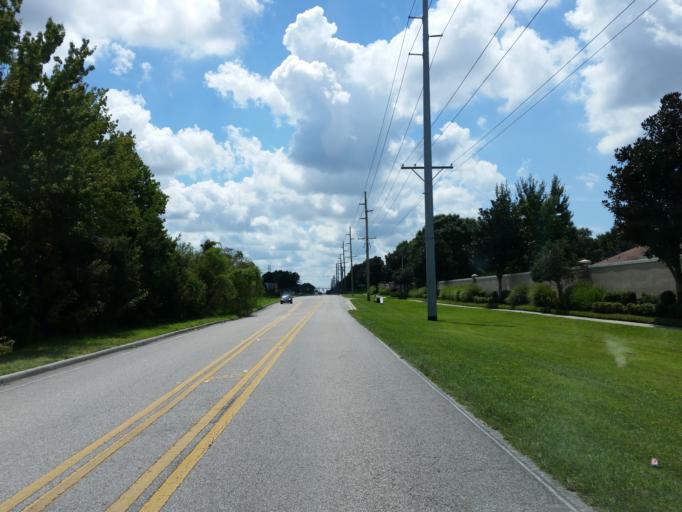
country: US
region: Florida
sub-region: Hillsborough County
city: Riverview
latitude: 27.8602
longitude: -82.3022
